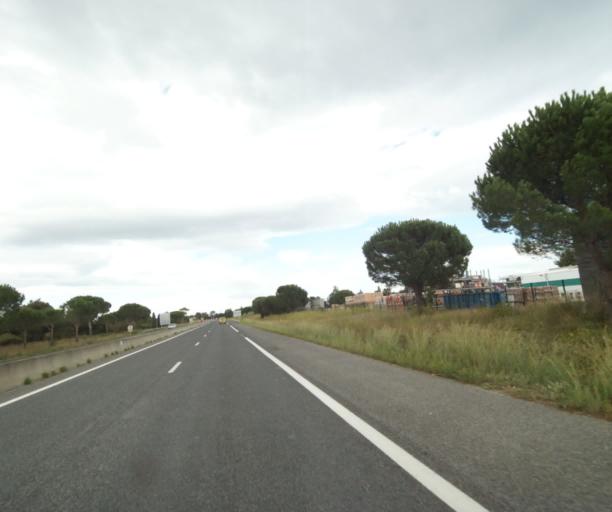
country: FR
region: Languedoc-Roussillon
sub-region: Departement des Pyrenees-Orientales
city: Argelers
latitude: 42.5572
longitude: 3.0062
